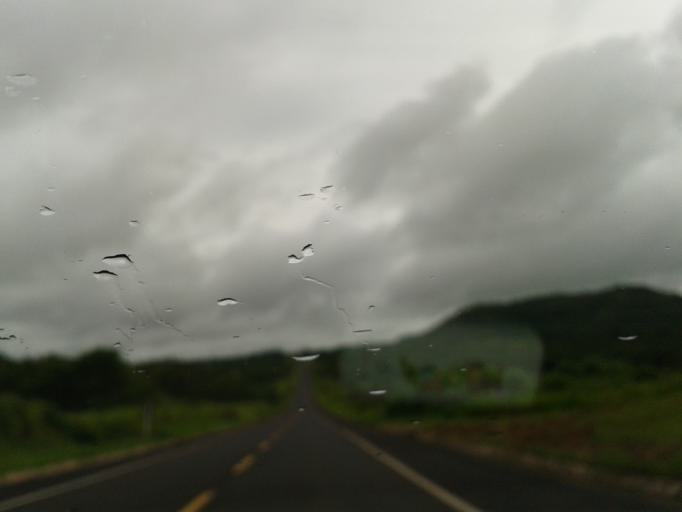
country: BR
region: Minas Gerais
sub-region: Santa Vitoria
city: Santa Vitoria
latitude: -19.2220
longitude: -50.0204
